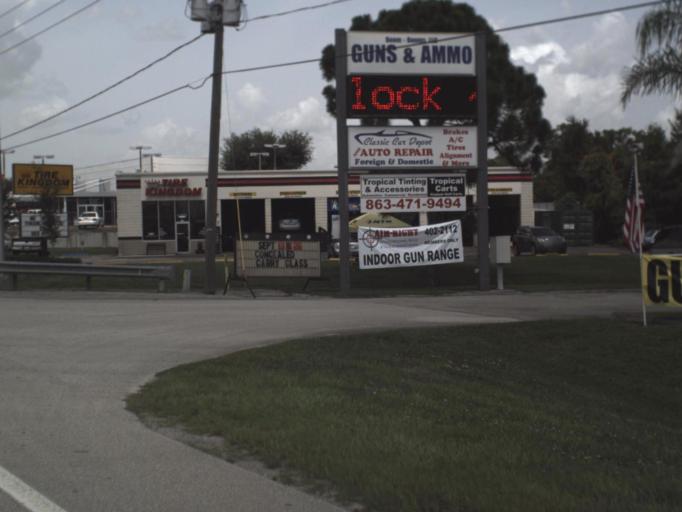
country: US
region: Florida
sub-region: Highlands County
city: Sebring
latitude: 27.4864
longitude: -81.4809
